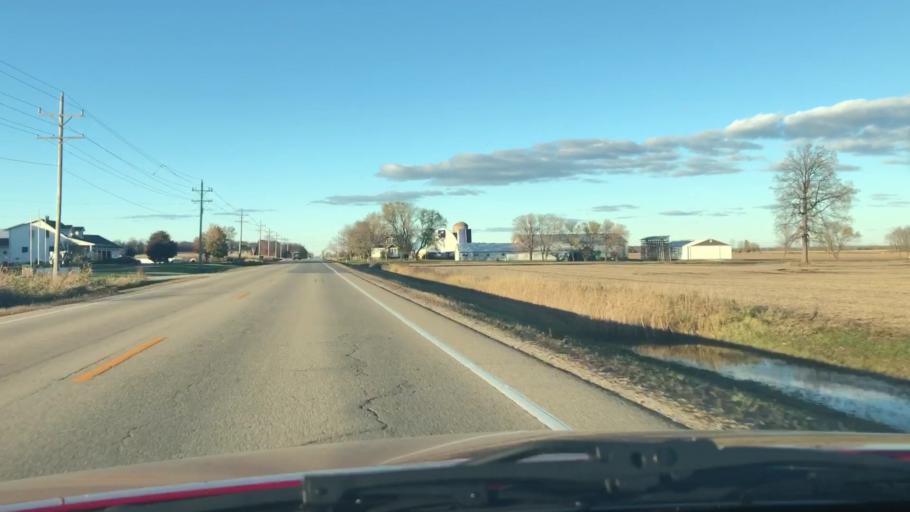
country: US
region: Wisconsin
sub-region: Outagamie County
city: Seymour
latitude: 44.4496
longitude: -88.2912
